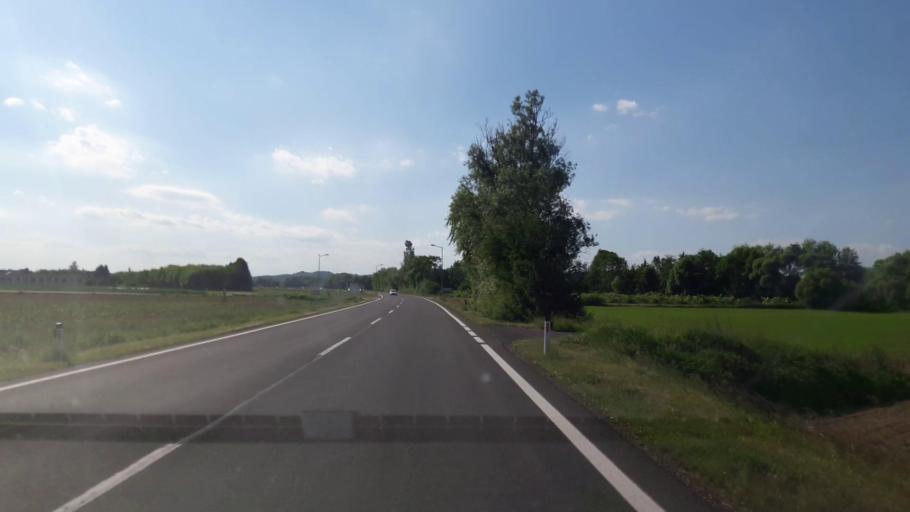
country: AT
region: Styria
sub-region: Politischer Bezirk Suedoststeiermark
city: Fehring
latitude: 46.9404
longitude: 16.0311
